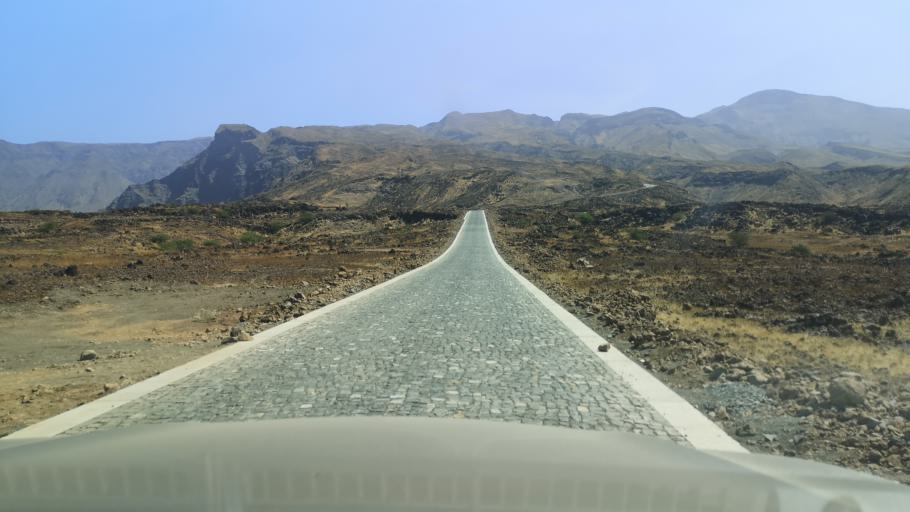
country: CV
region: Porto Novo
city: Porto Novo
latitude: 16.9422
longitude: -25.3137
